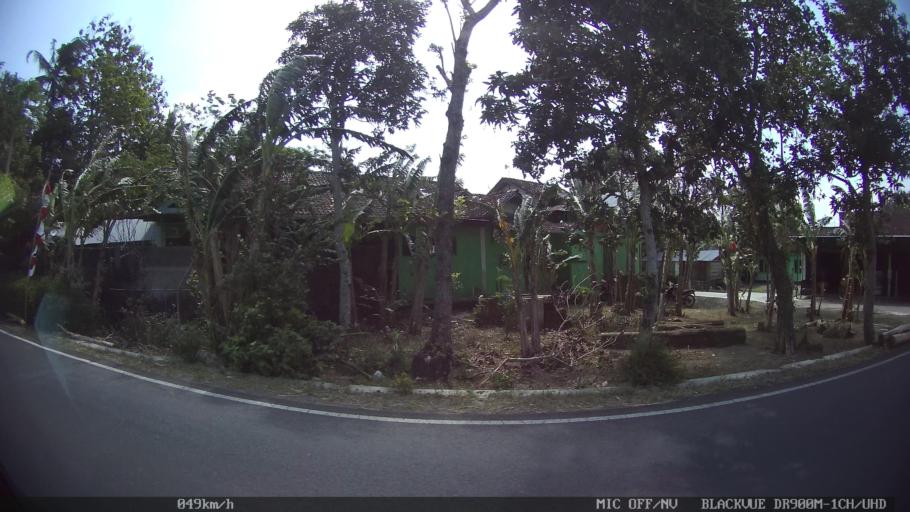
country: ID
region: Daerah Istimewa Yogyakarta
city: Pundong
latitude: -7.9820
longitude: 110.3361
